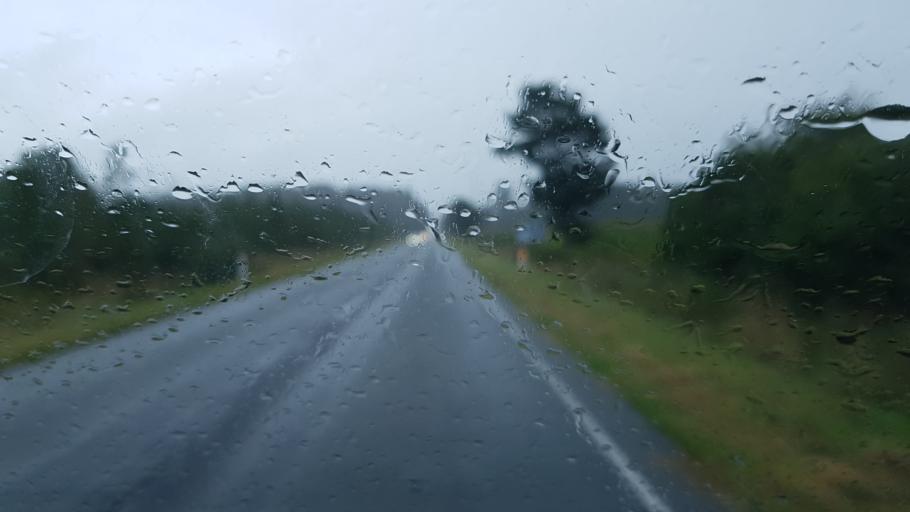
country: DK
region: South Denmark
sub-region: Kolding Kommune
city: Vamdrup
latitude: 55.3505
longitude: 9.2170
